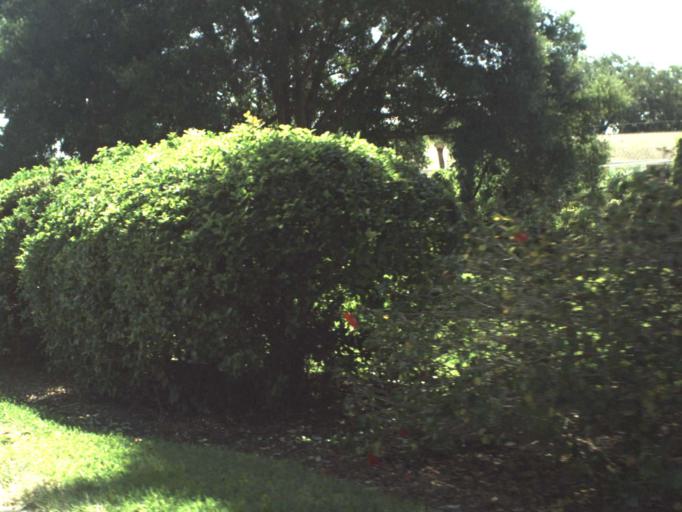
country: US
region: Florida
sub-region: Orange County
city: Conway
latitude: 28.5356
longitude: -81.3344
